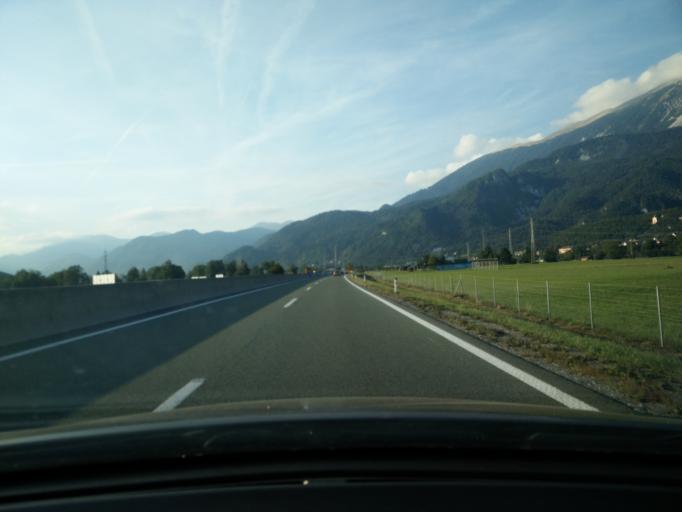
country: SI
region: Zirovnica
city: Zirovnica
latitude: 46.3942
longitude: 14.1343
